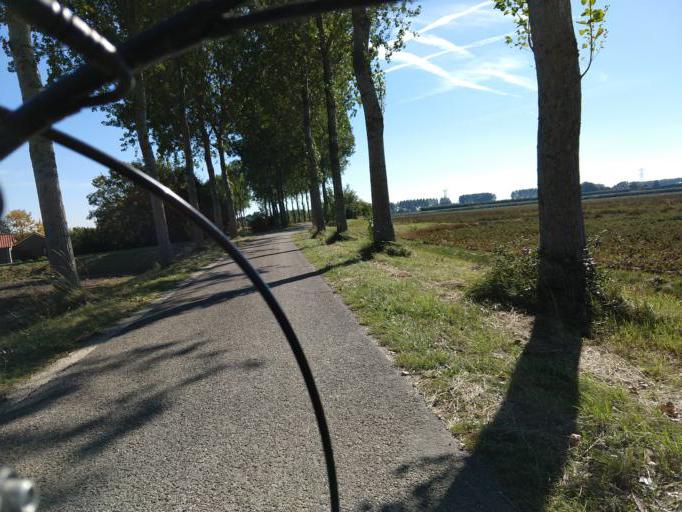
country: NL
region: Zeeland
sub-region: Gemeente Goes
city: Goes
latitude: 51.4270
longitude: 3.8416
